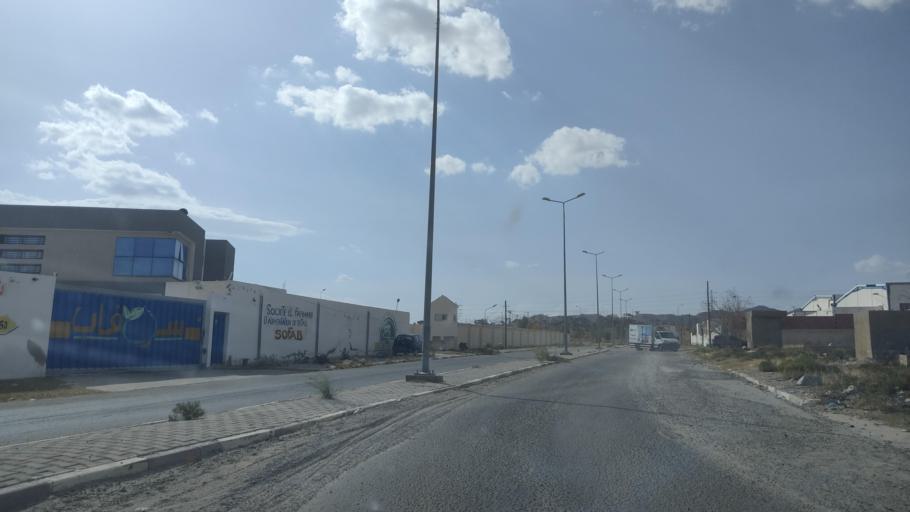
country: TN
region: Sidi Bu Zayd
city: Sidi Bouzid
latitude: 35.1080
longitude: 9.5434
